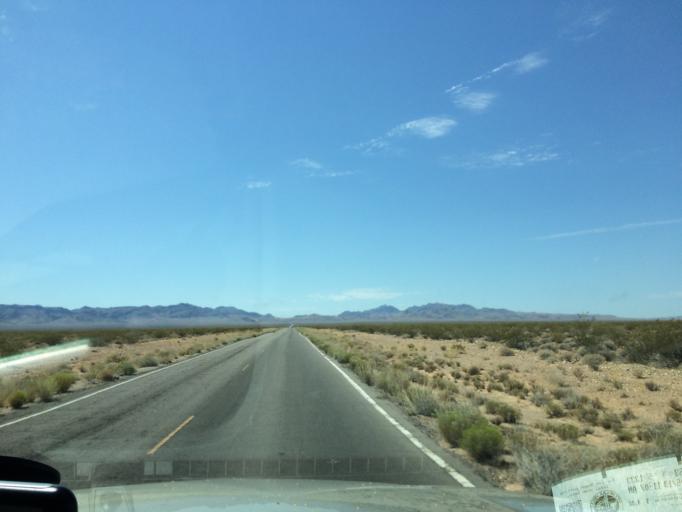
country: US
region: Nevada
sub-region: Clark County
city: Moapa Town
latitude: 36.4842
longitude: -114.7480
